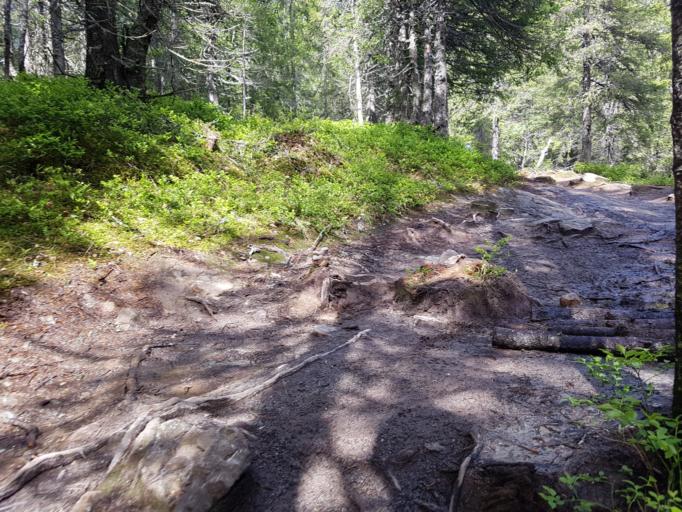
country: NO
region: Sor-Trondelag
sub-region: Trondheim
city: Trondheim
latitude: 63.4280
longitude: 10.3055
